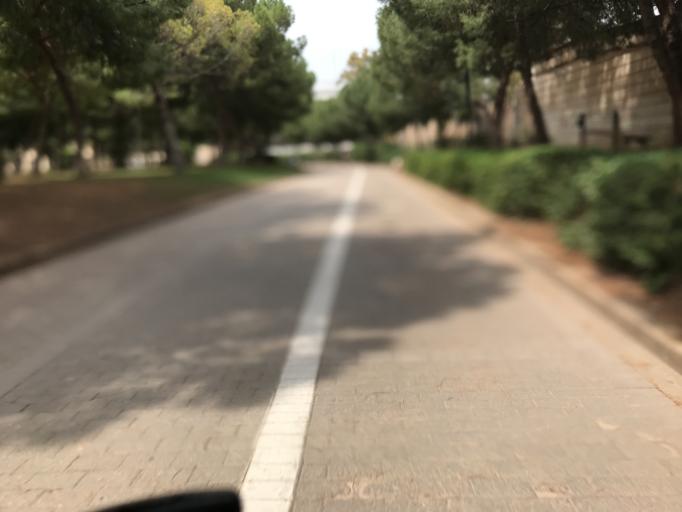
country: ES
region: Valencia
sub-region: Provincia de Valencia
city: Valencia
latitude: 39.4642
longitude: -0.3595
